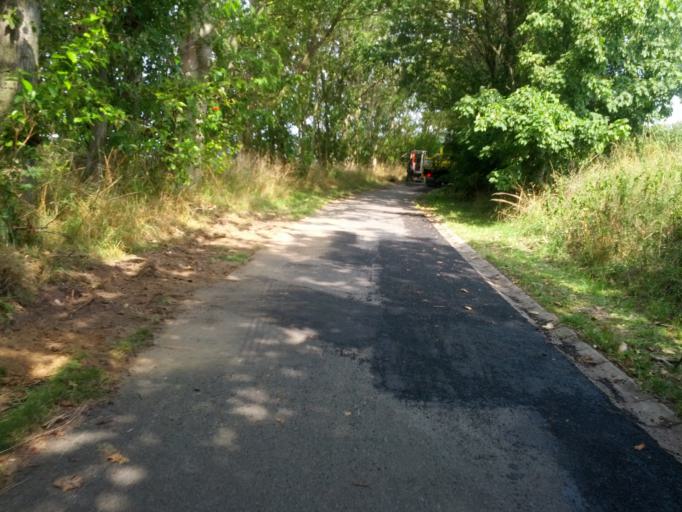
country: DE
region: Mecklenburg-Vorpommern
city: Bastorf
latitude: 54.1215
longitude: 11.6805
